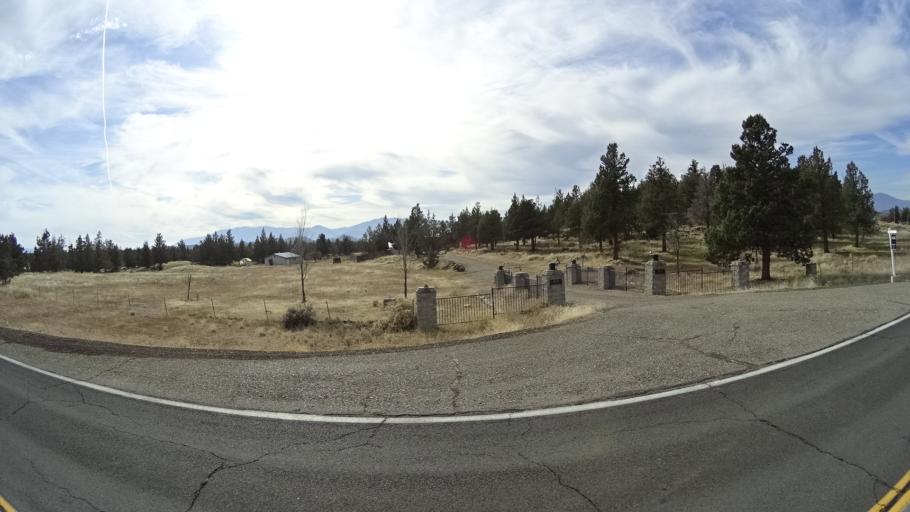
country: US
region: California
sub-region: Siskiyou County
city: Montague
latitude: 41.6079
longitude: -122.3979
